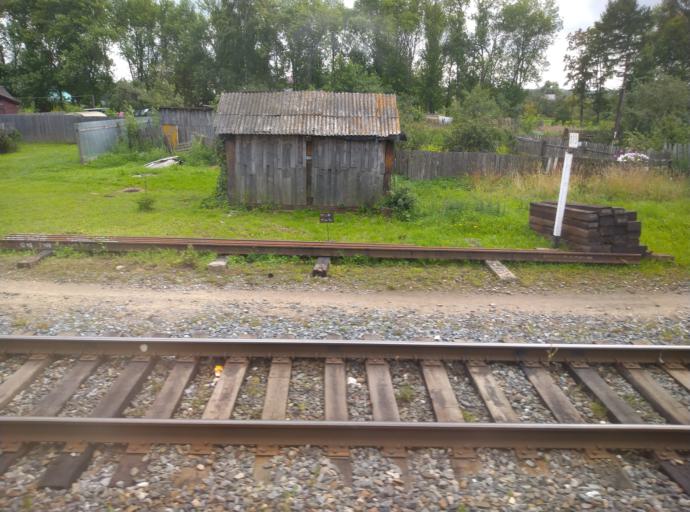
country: RU
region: Jaroslavl
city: Burmakino
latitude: 57.4368
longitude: 40.3172
